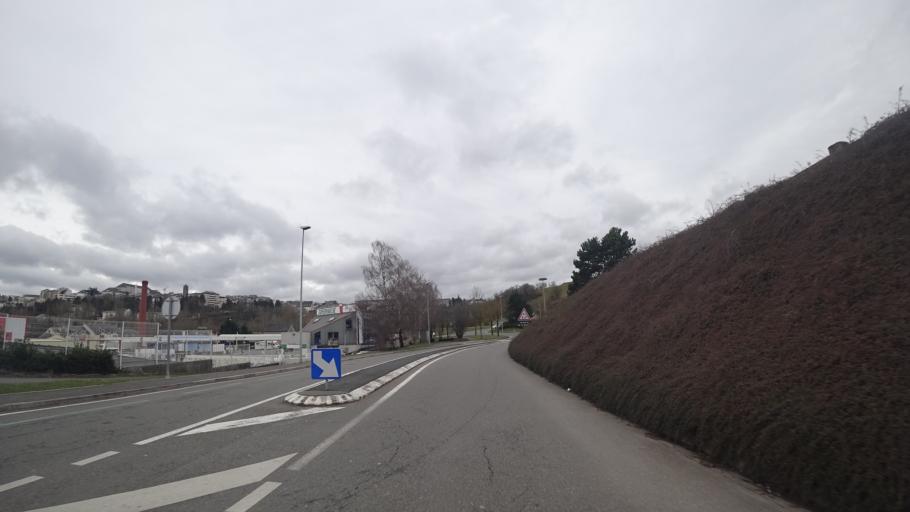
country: FR
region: Midi-Pyrenees
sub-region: Departement de l'Aveyron
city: Rodez
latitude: 44.3630
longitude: 2.5659
